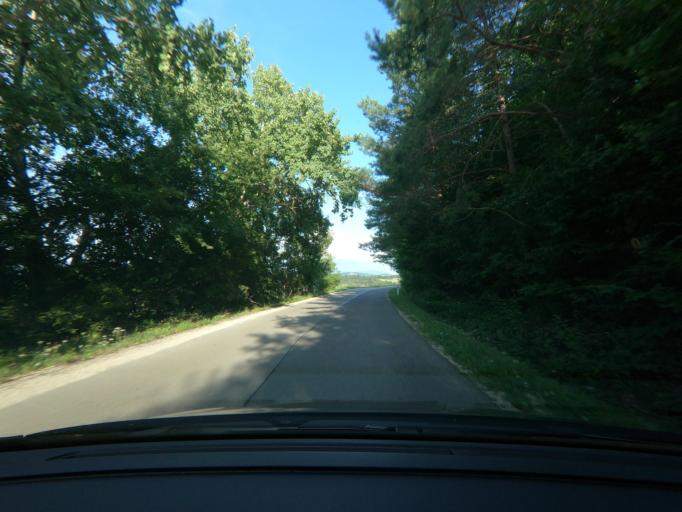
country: SK
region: Nitriansky
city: Stara Tura
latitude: 48.7274
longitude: 17.6769
